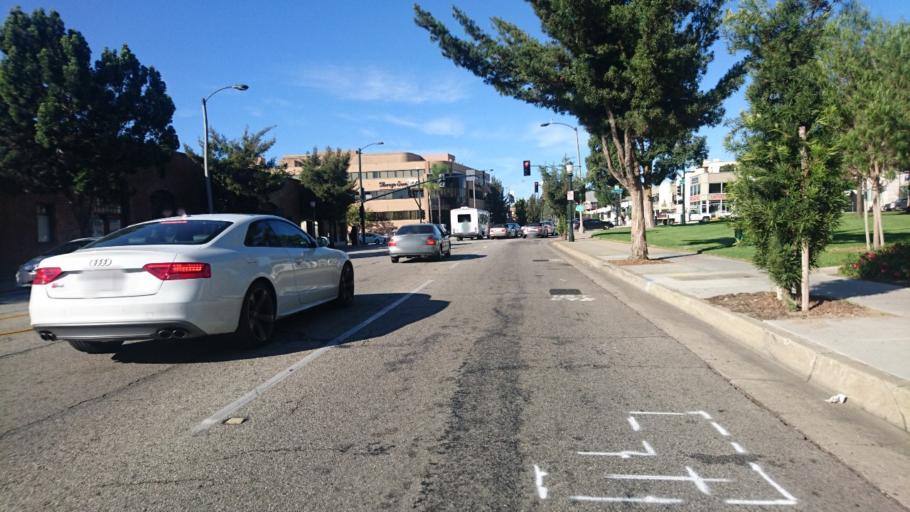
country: US
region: California
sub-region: Los Angeles County
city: Pasadena
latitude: 34.1407
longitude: -118.1496
